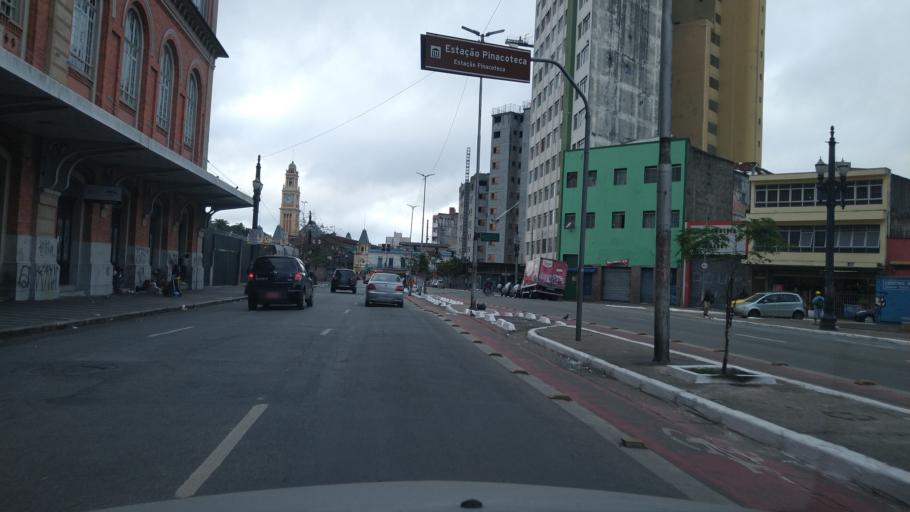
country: BR
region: Sao Paulo
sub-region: Sao Paulo
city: Sao Paulo
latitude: -23.5350
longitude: -46.6388
